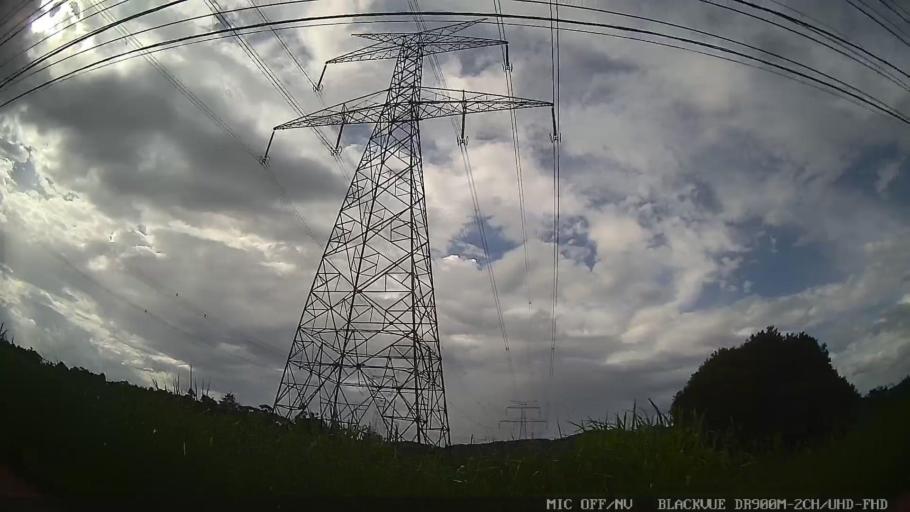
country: BR
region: Sao Paulo
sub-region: Mogi das Cruzes
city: Mogi das Cruzes
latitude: -23.5431
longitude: -46.2449
